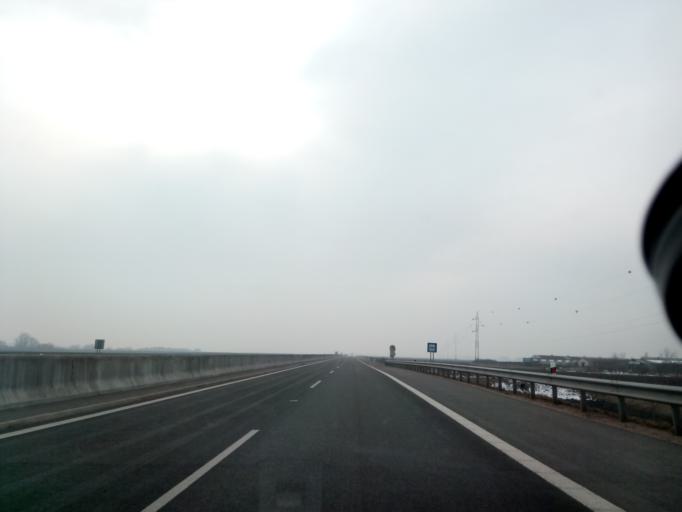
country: SK
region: Kosicky
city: Kosice
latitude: 48.6118
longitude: 21.2413
